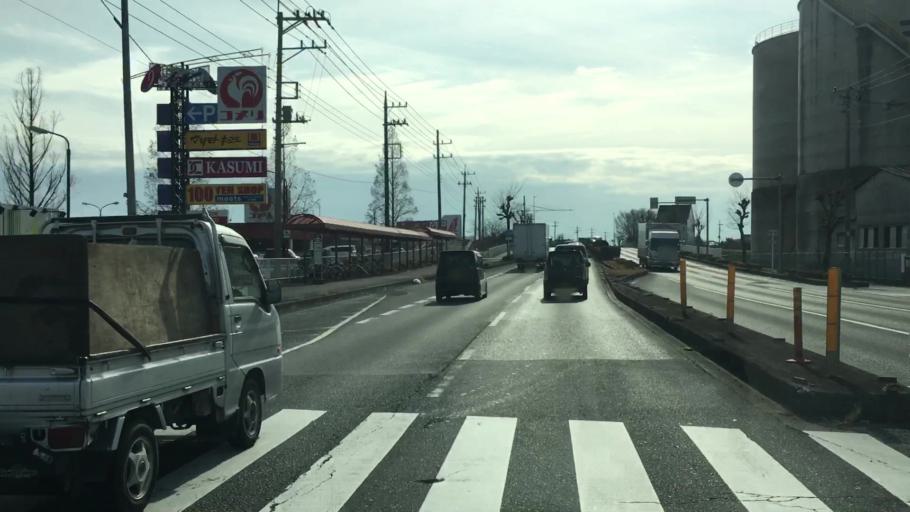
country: JP
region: Saitama
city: Menuma
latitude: 36.2100
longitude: 139.3701
